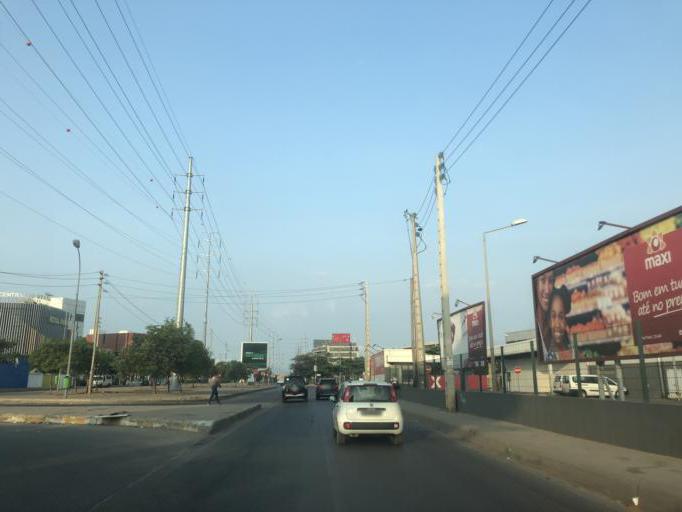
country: AO
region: Luanda
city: Luanda
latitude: -8.9037
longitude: 13.1919
